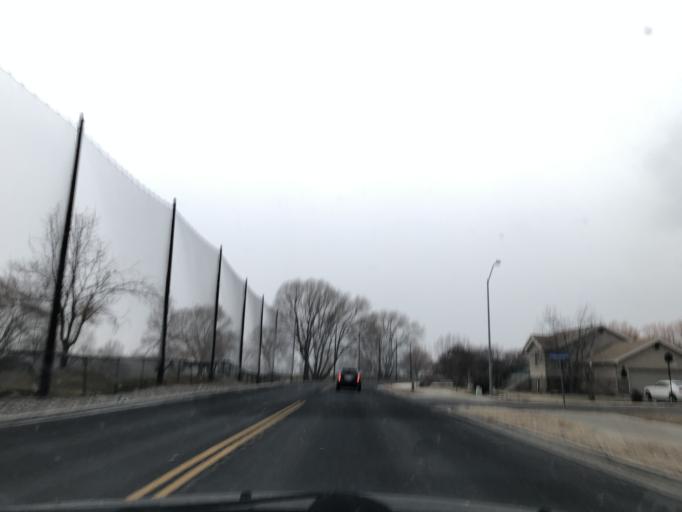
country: US
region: Utah
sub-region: Cache County
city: Logan
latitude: 41.7152
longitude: -111.8437
